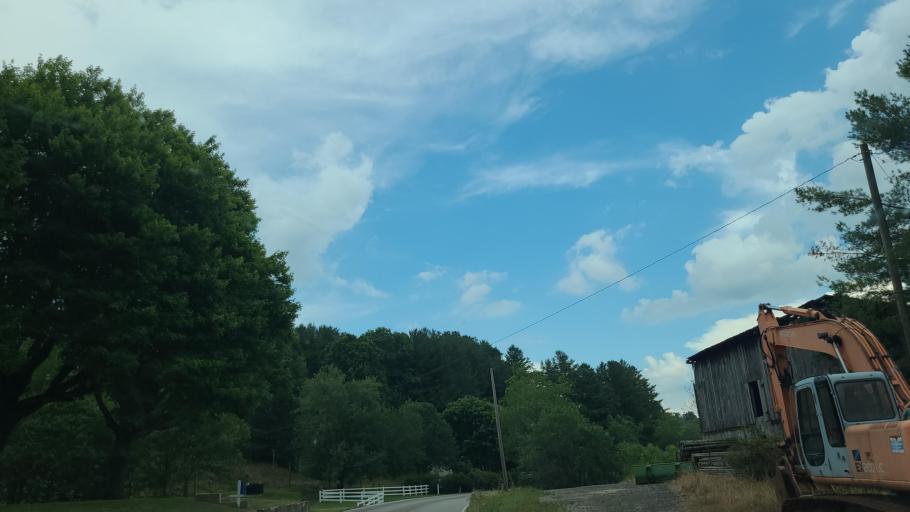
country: US
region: North Carolina
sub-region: Alleghany County
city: Sparta
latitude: 36.4173
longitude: -81.2677
